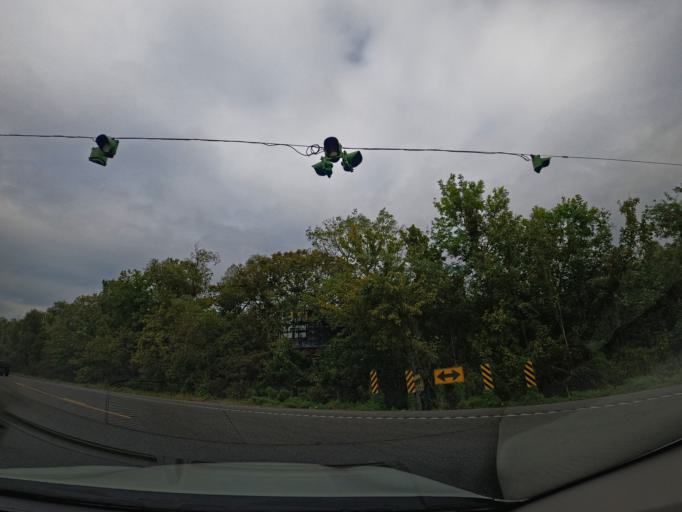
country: US
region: Louisiana
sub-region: Saint Mary Parish
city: Amelia
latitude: 29.6863
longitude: -91.0011
